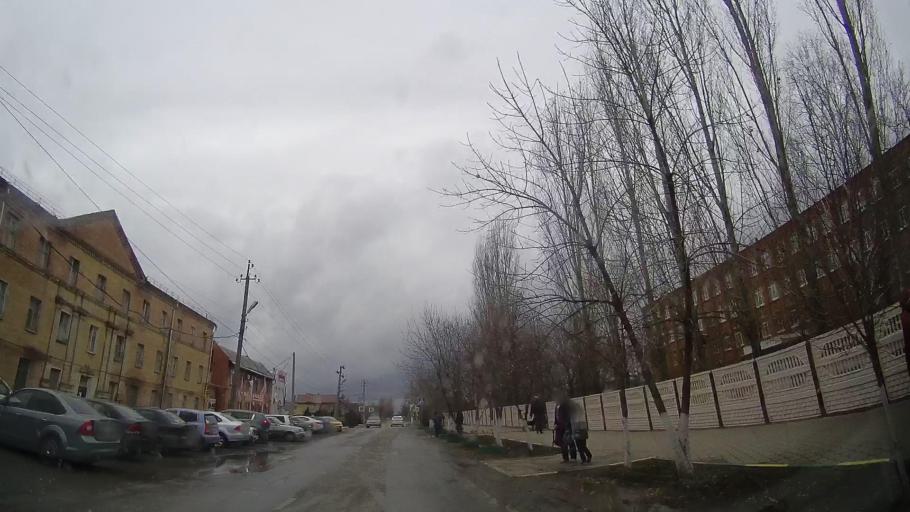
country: RU
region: Rostov
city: Bataysk
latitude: 47.1150
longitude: 39.7450
